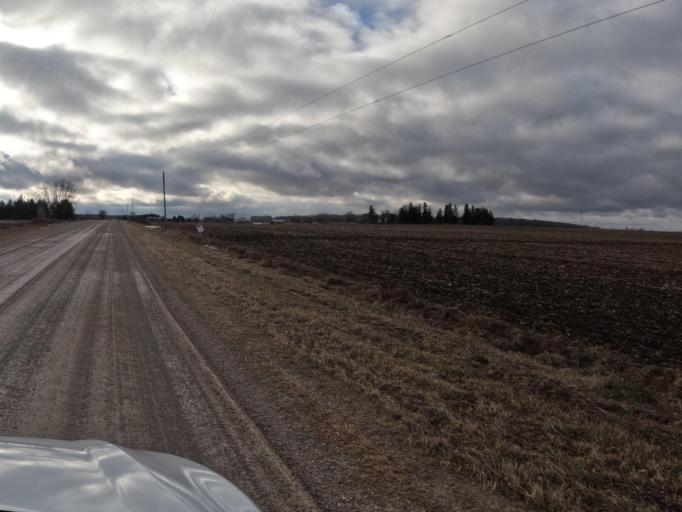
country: CA
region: Ontario
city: Shelburne
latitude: 43.8844
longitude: -80.3588
